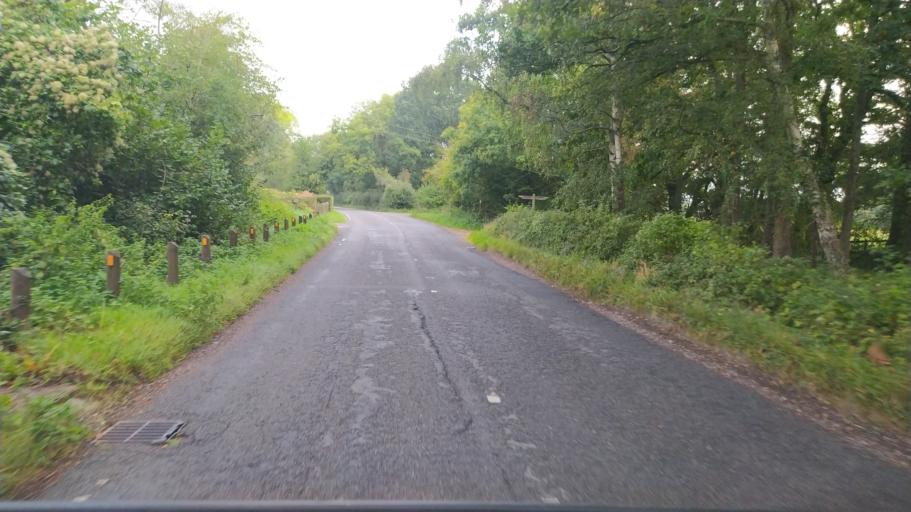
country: GB
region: England
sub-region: Hampshire
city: East Dean
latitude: 51.0456
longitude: -1.5506
